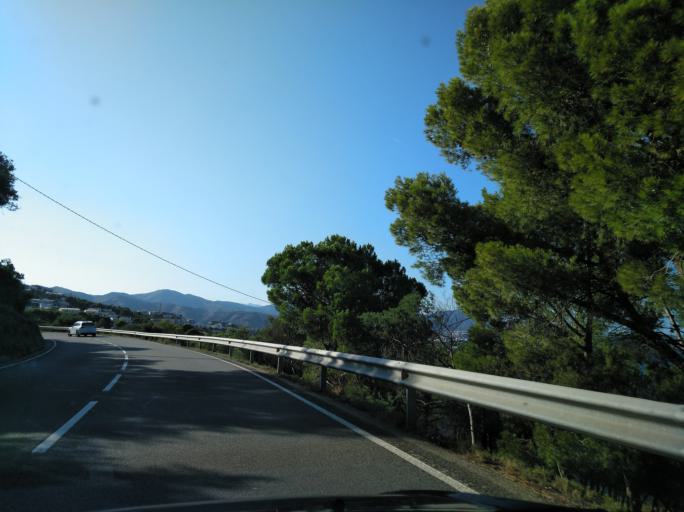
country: ES
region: Catalonia
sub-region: Provincia de Girona
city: Llanca
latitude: 42.3541
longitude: 3.1739
